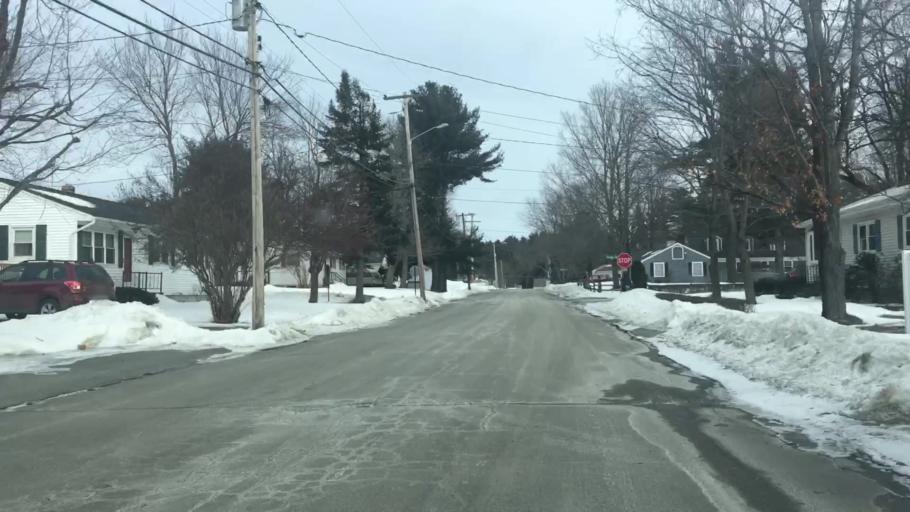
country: US
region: Maine
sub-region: Kennebec County
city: Augusta
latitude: 44.3065
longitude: -69.7578
